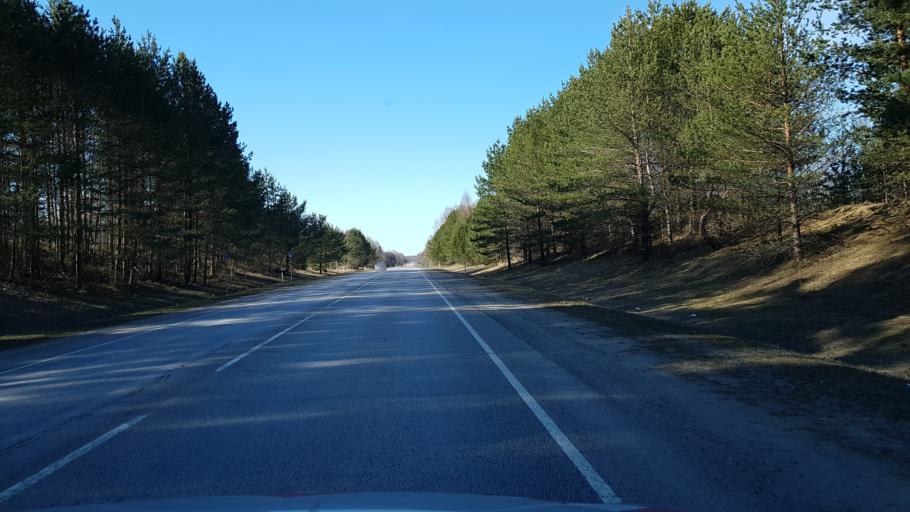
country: EE
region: Ida-Virumaa
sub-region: Johvi vald
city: Johvi
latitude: 59.1656
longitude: 27.3526
